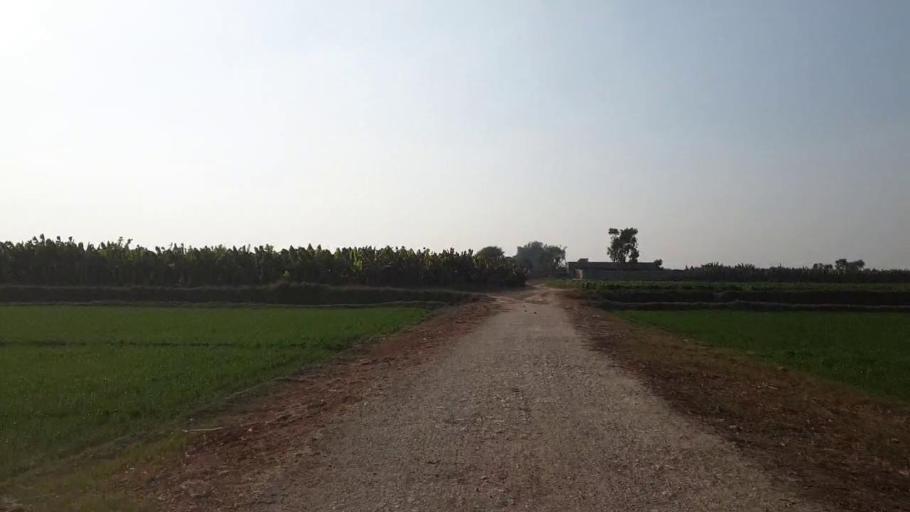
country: PK
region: Sindh
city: Matiari
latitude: 25.5995
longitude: 68.5906
